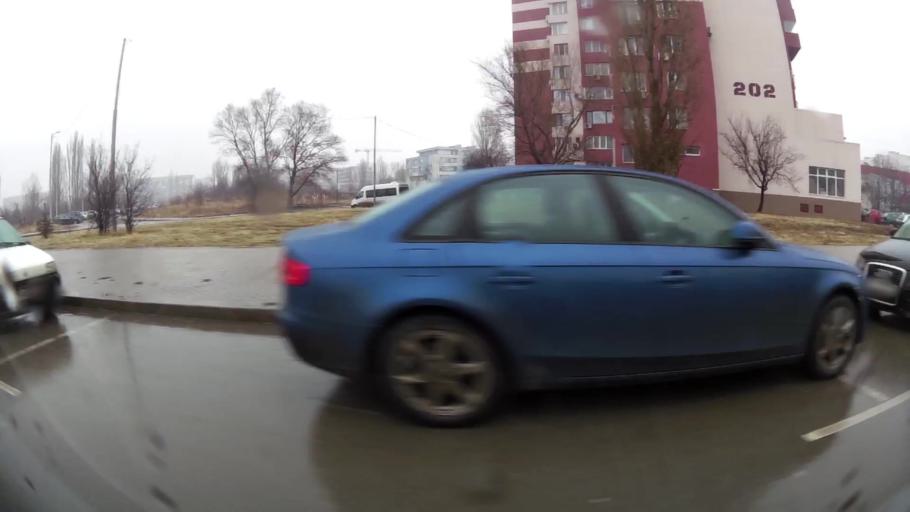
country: BG
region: Sofia-Capital
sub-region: Stolichna Obshtina
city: Sofia
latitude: 42.6549
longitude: 23.3953
